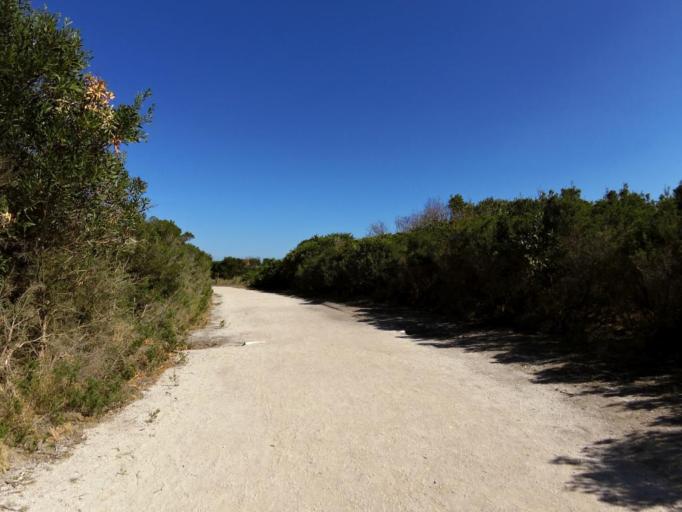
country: AU
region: Victoria
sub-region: Bass Coast
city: North Wonthaggi
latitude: -38.5492
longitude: 145.4672
